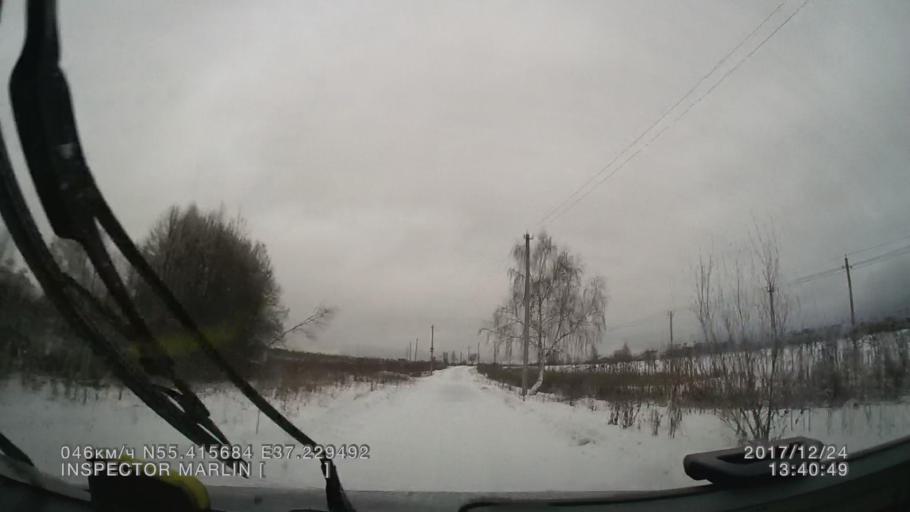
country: RU
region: Moskovskaya
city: Troitsk
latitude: 55.4157
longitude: 37.2296
